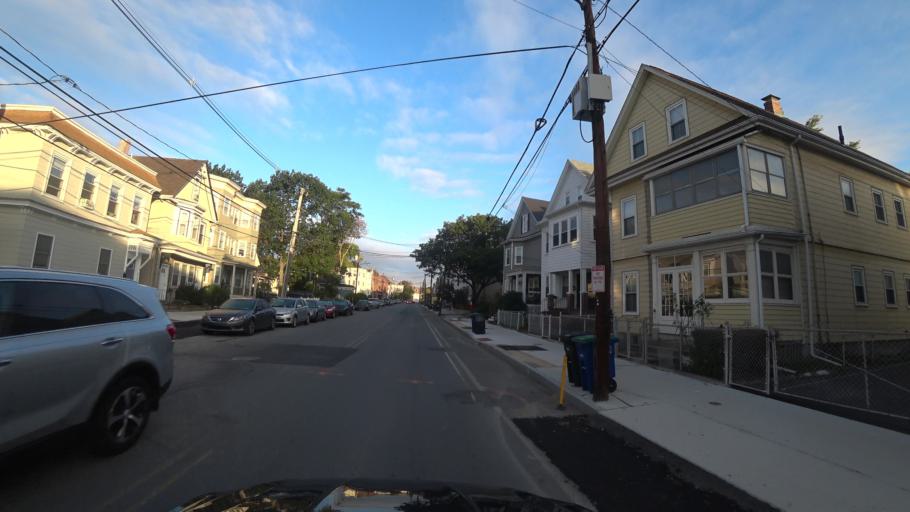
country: US
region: Massachusetts
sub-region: Middlesex County
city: Cambridge
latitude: 42.3844
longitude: -71.1139
